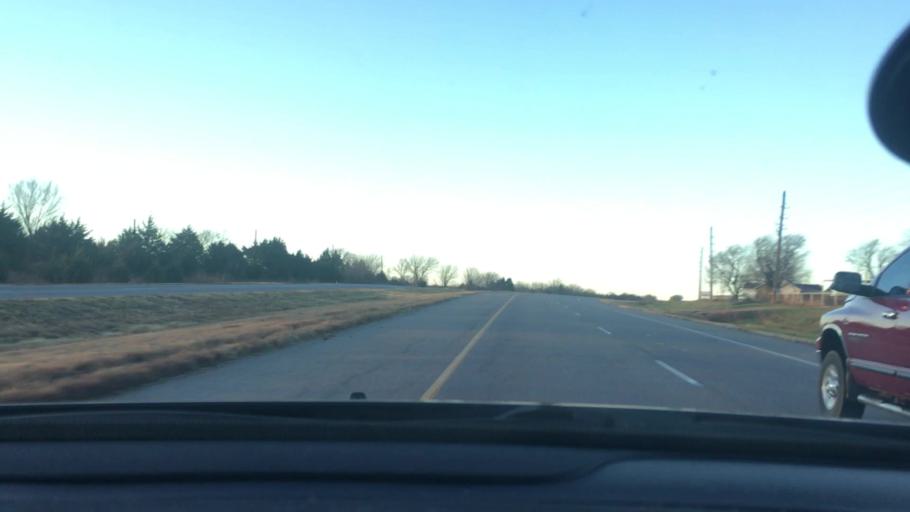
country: US
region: Oklahoma
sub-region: Pontotoc County
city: Ada
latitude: 34.7220
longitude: -96.7154
